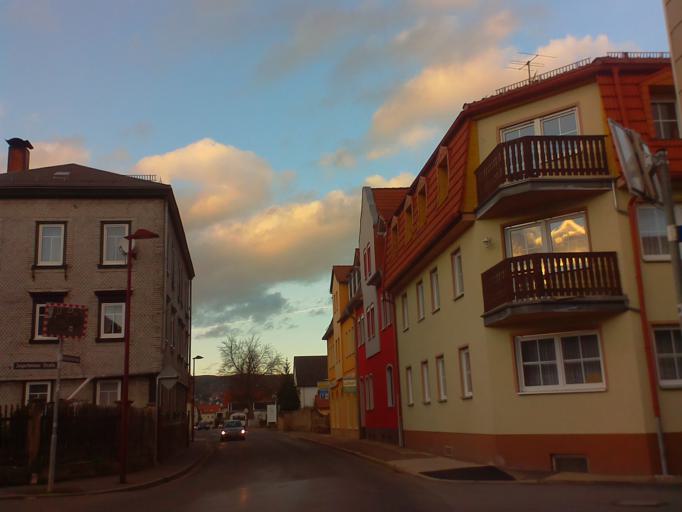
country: DE
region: Thuringia
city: Rudolstadt
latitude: 50.7048
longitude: 11.3246
